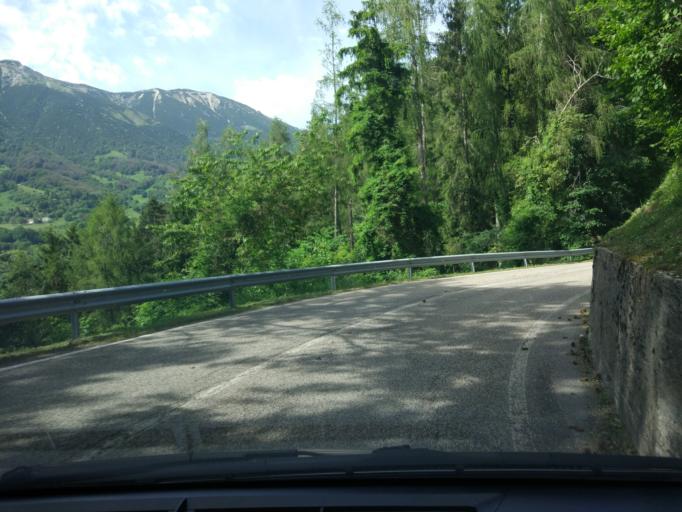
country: IT
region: Veneto
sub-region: Provincia di Verona
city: Ferrara di Monte Baldo
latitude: 45.6749
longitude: 10.8589
